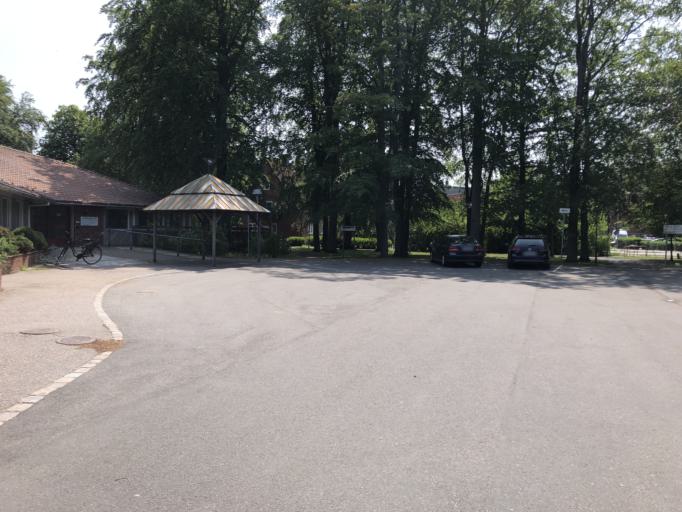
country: SE
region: Skane
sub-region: Lunds Kommun
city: Lund
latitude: 55.7159
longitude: 13.1992
